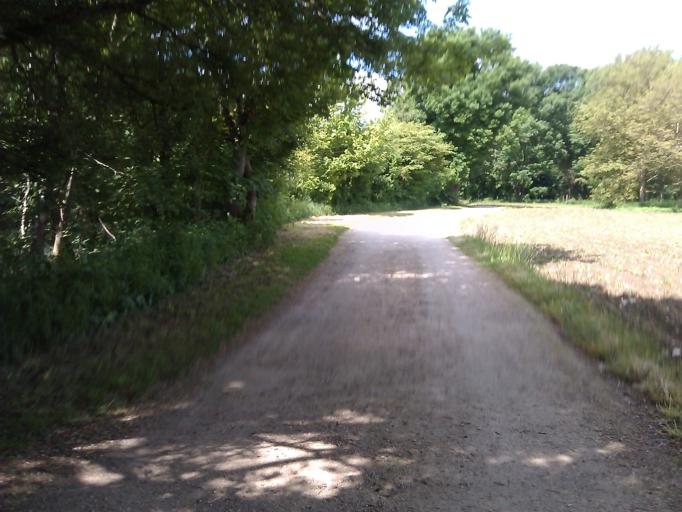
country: FR
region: Poitou-Charentes
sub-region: Departement de la Charente
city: Fleac
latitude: 45.6716
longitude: 0.1083
